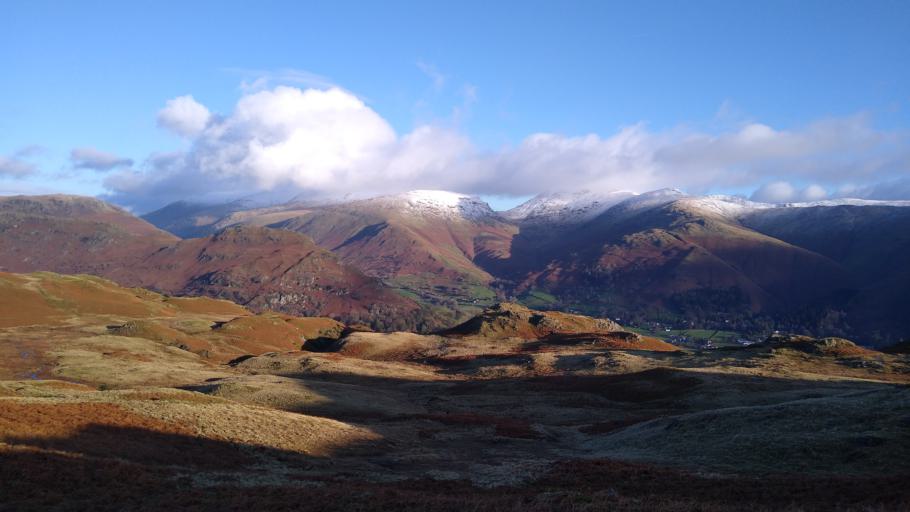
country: GB
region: England
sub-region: Cumbria
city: Ambleside
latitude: 54.4513
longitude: -3.0463
